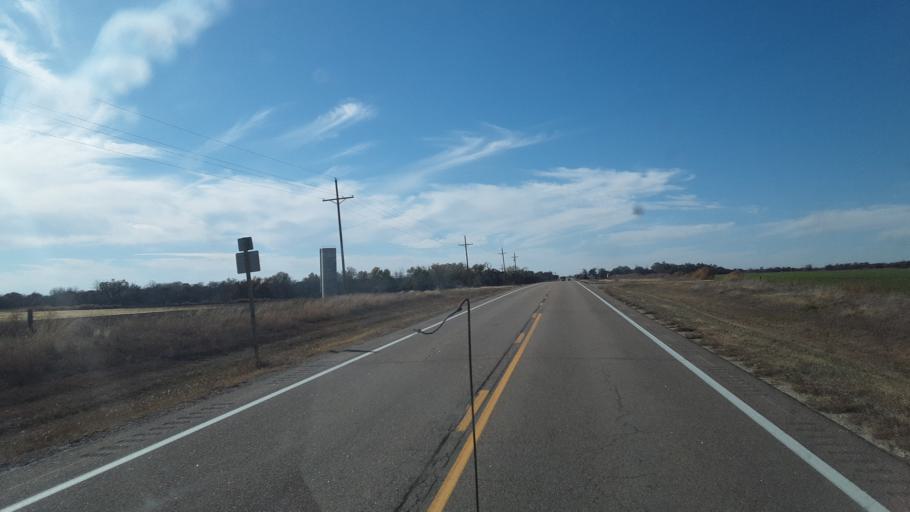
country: US
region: Kansas
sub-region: Pawnee County
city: Larned
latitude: 38.1896
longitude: -99.3176
